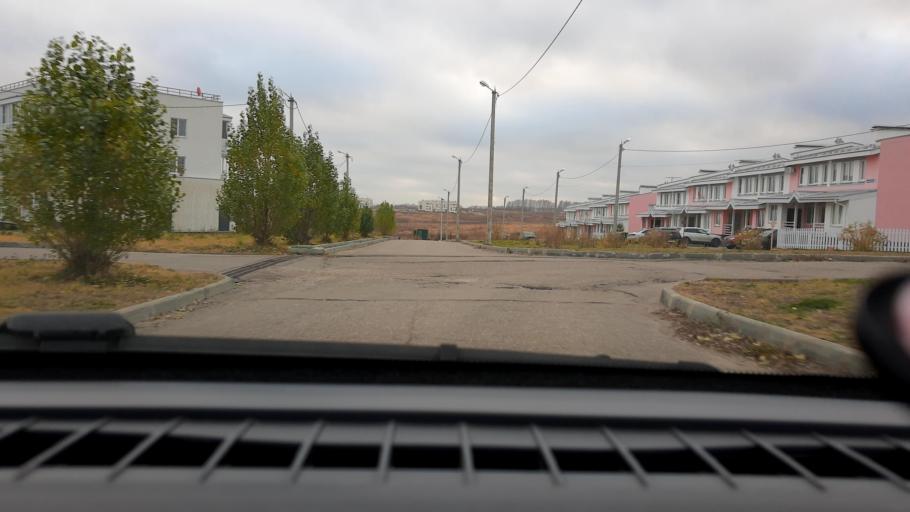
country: RU
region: Nizjnij Novgorod
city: Burevestnik
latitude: 56.1901
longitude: 43.8605
